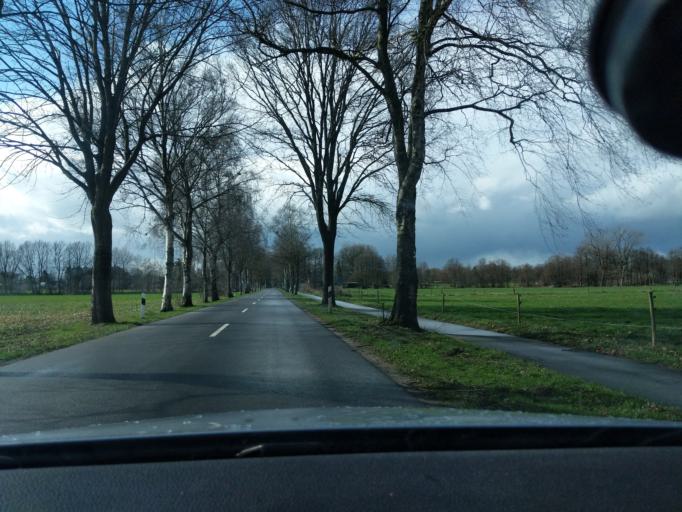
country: DE
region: Lower Saxony
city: Kranenburg
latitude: 53.6073
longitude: 9.2186
